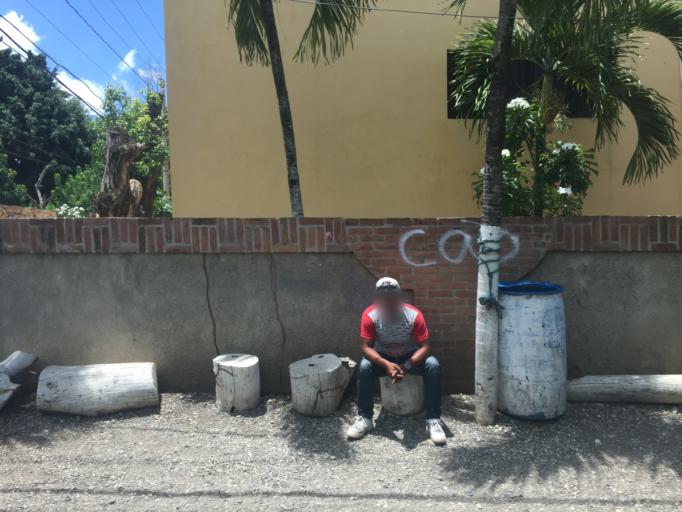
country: DO
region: Santiago
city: Santiago de los Caballeros
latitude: 19.4784
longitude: -70.6671
